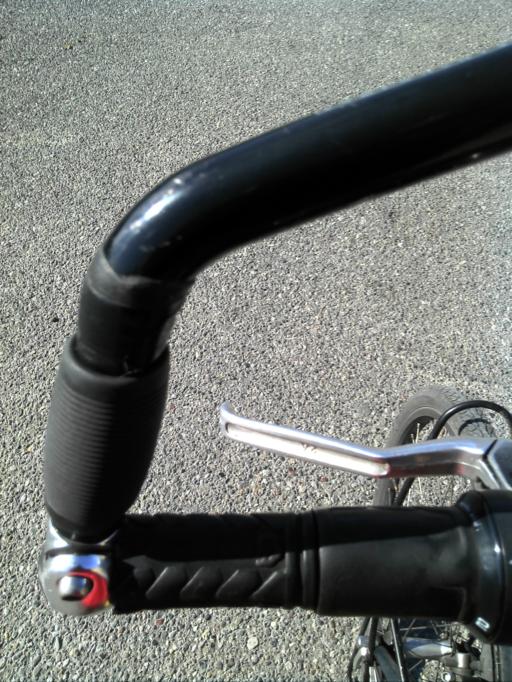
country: AL
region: Shkoder
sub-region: Rrethi i Shkodres
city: Dajc
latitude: 42.0156
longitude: 19.4284
